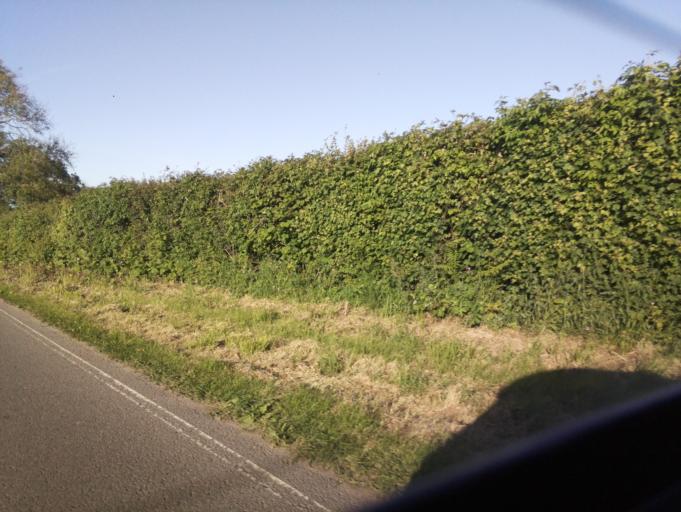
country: GB
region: England
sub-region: Devon
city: Sidmouth
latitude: 50.7142
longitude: -3.1665
